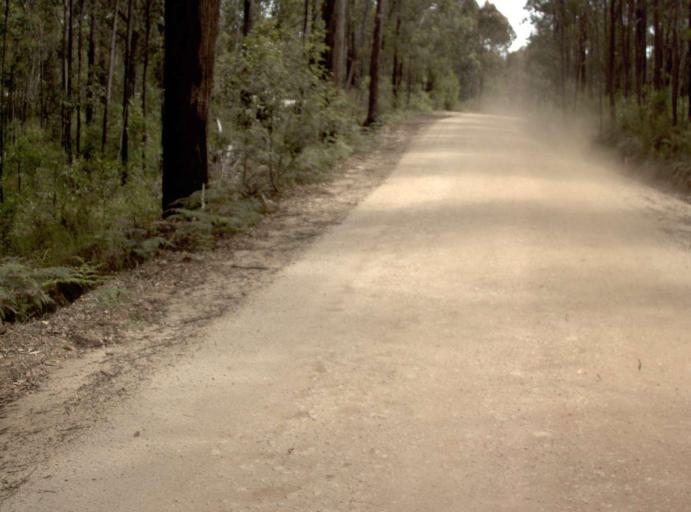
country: AU
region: Victoria
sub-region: East Gippsland
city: Lakes Entrance
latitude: -37.6875
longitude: 148.6192
